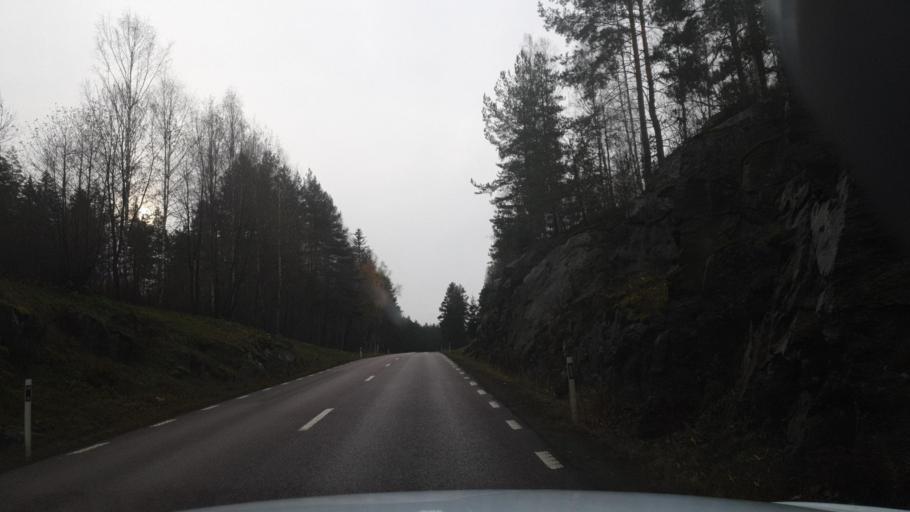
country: SE
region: Vaermland
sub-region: Arvika Kommun
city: Arvika
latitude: 59.6339
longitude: 12.6177
